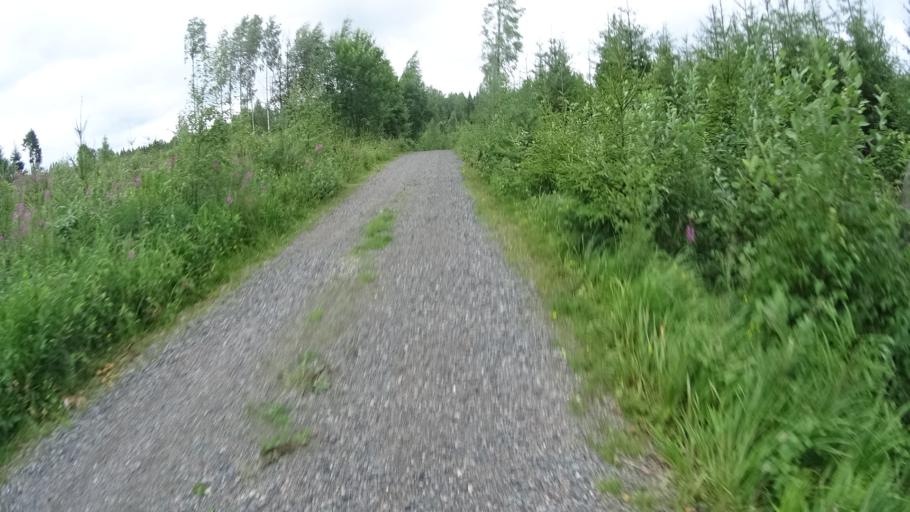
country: FI
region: Uusimaa
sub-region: Helsinki
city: Karkkila
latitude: 60.5636
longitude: 24.3319
